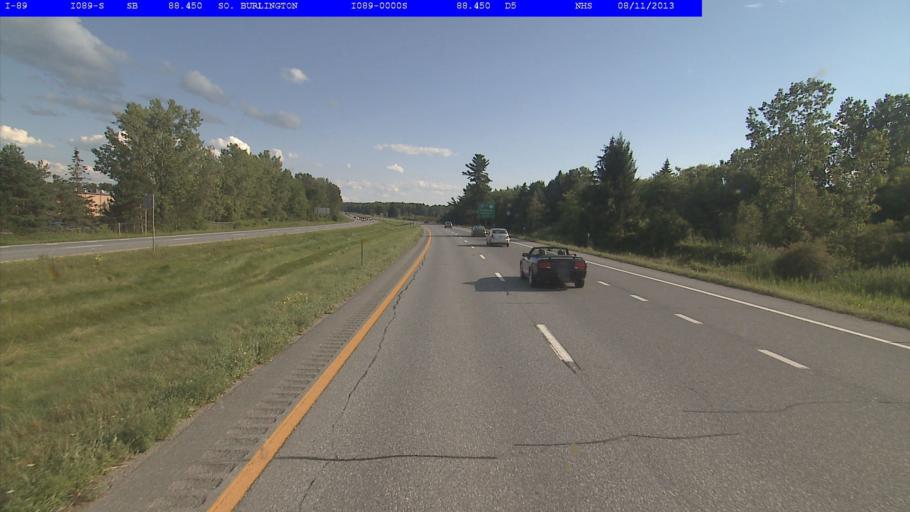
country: US
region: Vermont
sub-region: Chittenden County
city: South Burlington
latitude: 44.4662
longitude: -73.1857
